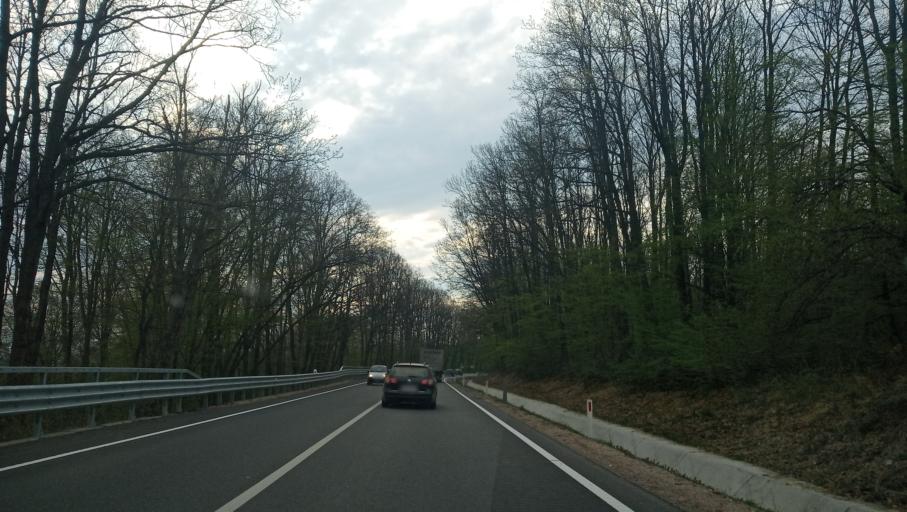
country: RO
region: Bihor
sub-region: Comuna Rabagani
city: Rabagani
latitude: 46.7227
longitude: 22.2442
